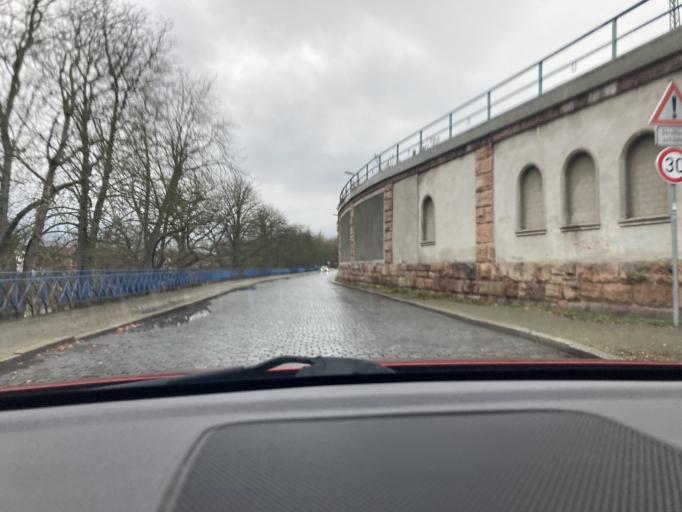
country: DE
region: Saxony-Anhalt
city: Weissenfels
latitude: 51.2041
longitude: 11.9705
